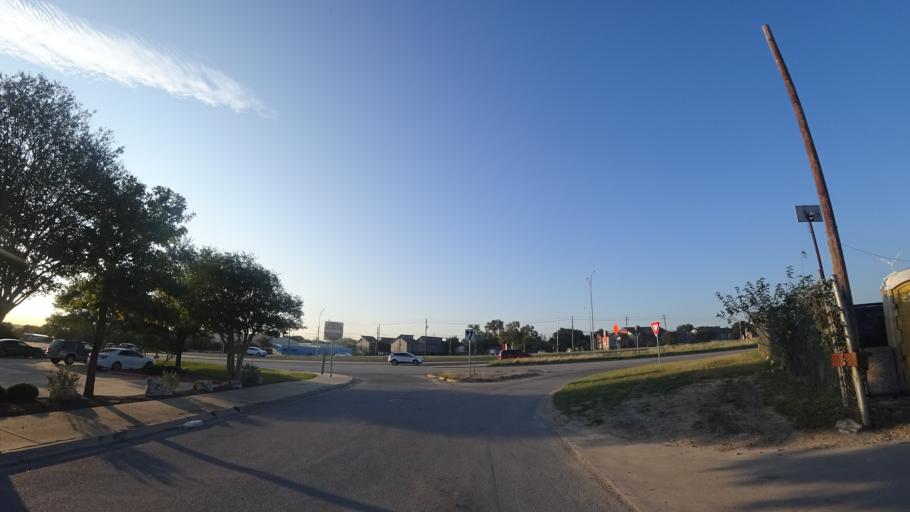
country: US
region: Texas
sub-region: Travis County
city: Austin
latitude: 30.3222
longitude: -97.6860
